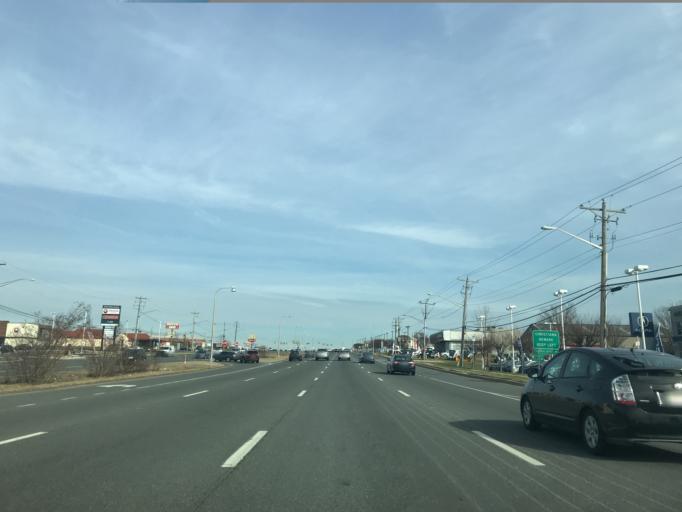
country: US
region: Delaware
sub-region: New Castle County
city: Wilmington Manor
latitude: 39.6627
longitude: -75.6069
